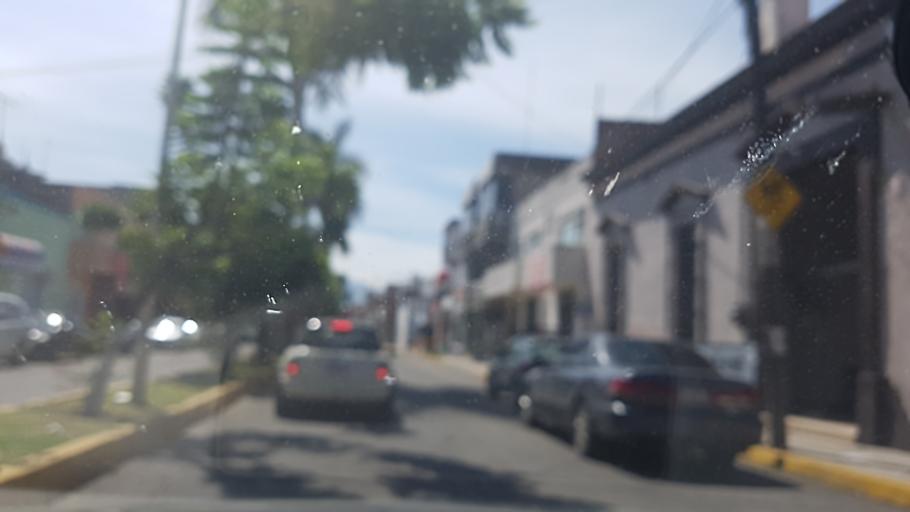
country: MX
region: Nayarit
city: Tepic
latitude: 21.5108
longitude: -104.8986
